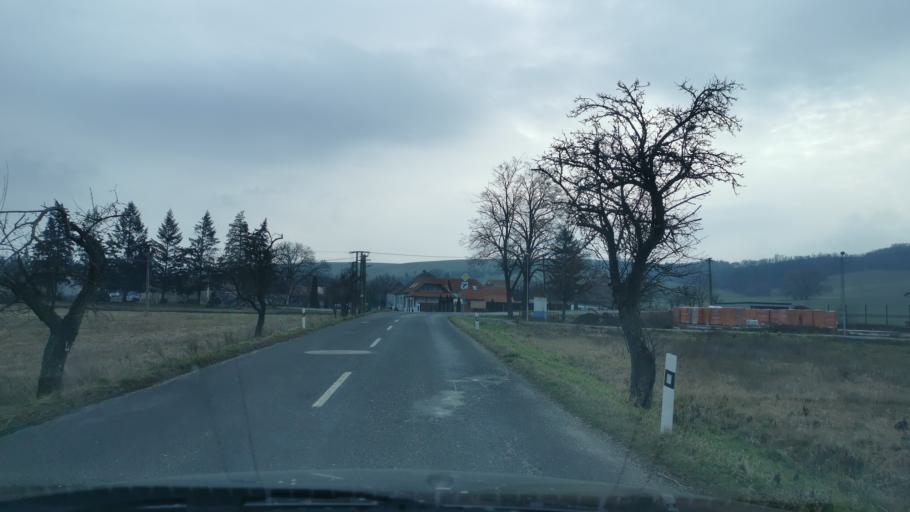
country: SK
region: Trnavsky
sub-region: Okres Senica
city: Senica
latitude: 48.7461
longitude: 17.3006
